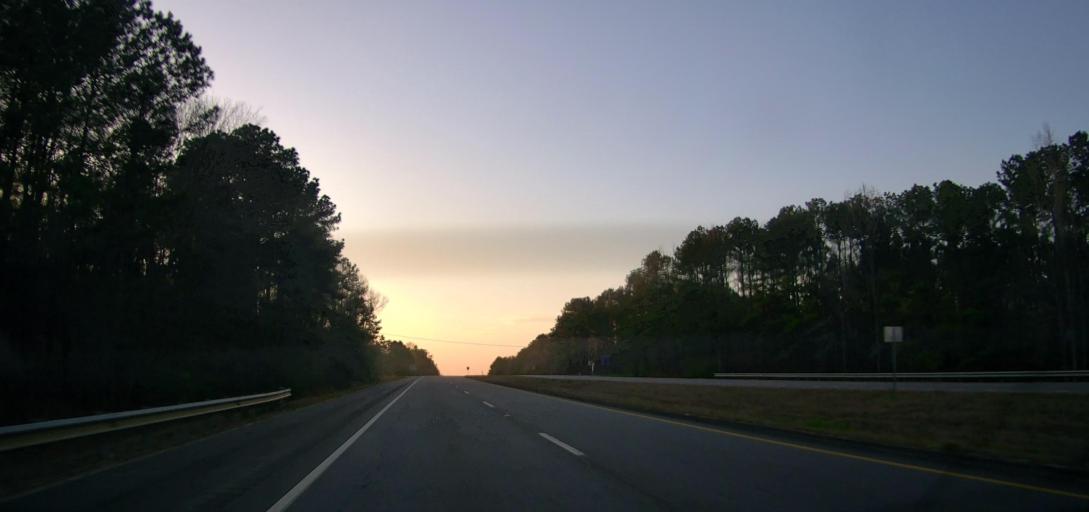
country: US
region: Alabama
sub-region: Coosa County
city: Goodwater
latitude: 33.0188
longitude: -86.1026
